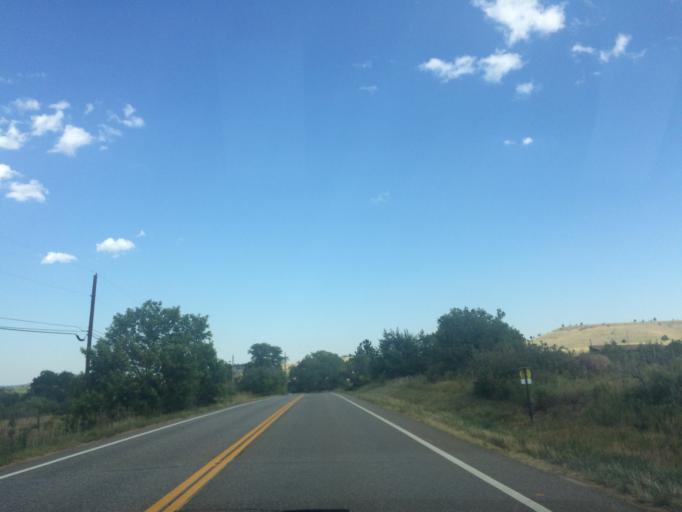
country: US
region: Colorado
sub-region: Boulder County
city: Boulder
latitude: 39.9357
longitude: -105.2677
